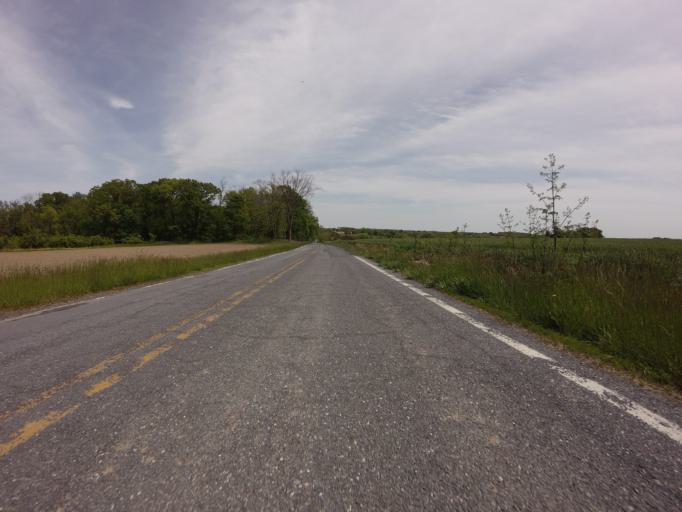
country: US
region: Maryland
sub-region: Frederick County
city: Linganore
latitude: 39.5100
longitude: -77.2088
